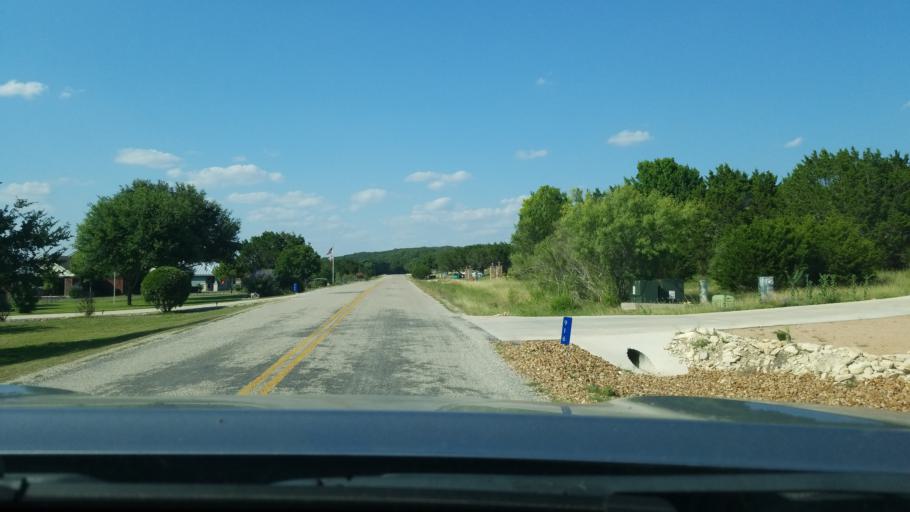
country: US
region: Texas
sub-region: Comal County
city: Bulverde
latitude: 29.8268
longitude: -98.3993
